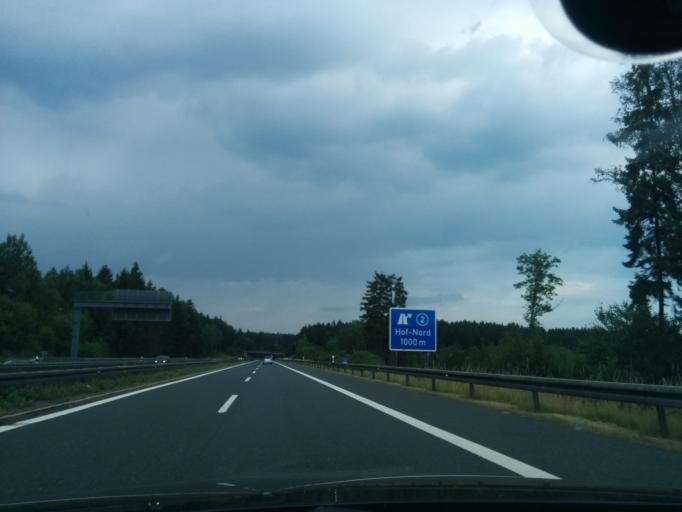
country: DE
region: Bavaria
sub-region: Upper Franconia
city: Koditz
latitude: 50.3359
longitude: 11.8157
